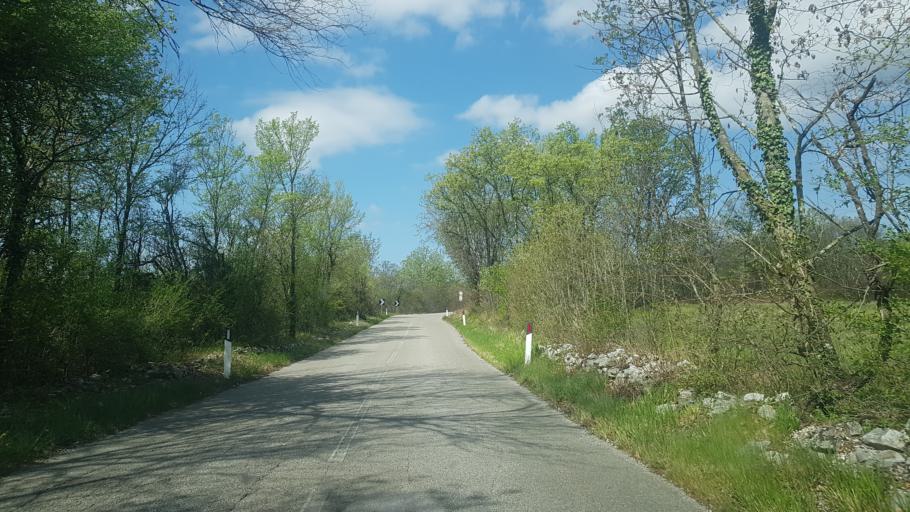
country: IT
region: Friuli Venezia Giulia
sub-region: Provincia di Gorizia
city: Doberdo del Lago
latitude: 45.8682
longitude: 13.5424
